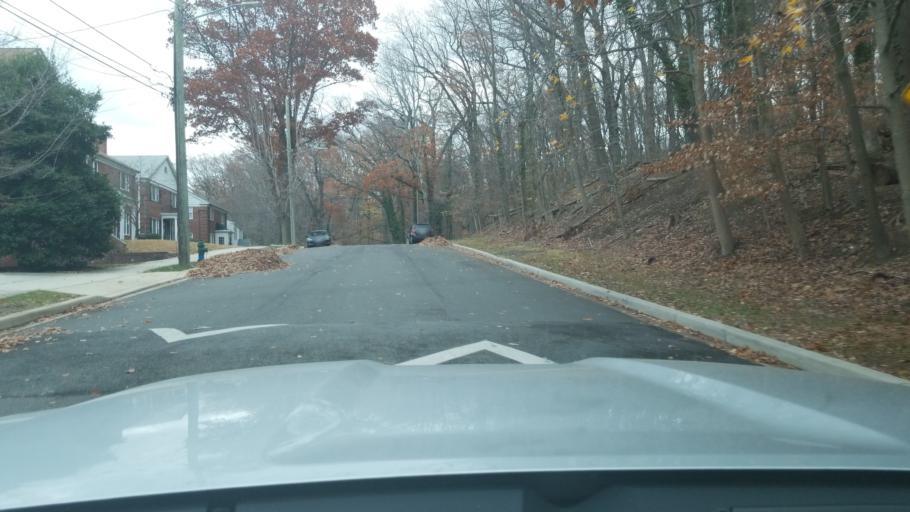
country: US
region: Maryland
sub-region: Prince George's County
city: Silver Hill
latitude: 38.8690
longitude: -76.9518
